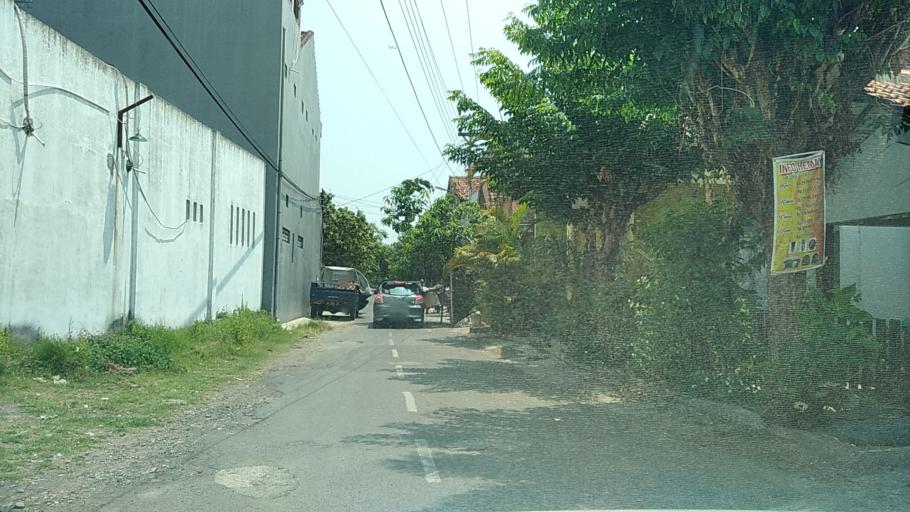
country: ID
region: Central Java
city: Mranggen
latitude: -7.0206
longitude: 110.4801
